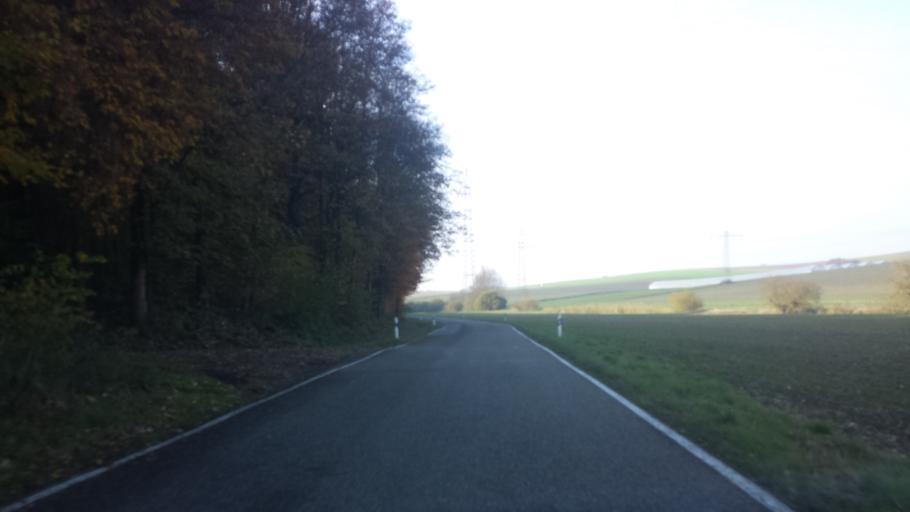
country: DE
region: Baden-Wuerttemberg
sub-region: Karlsruhe Region
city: Aglasterhausen
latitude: 49.3181
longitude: 9.0109
